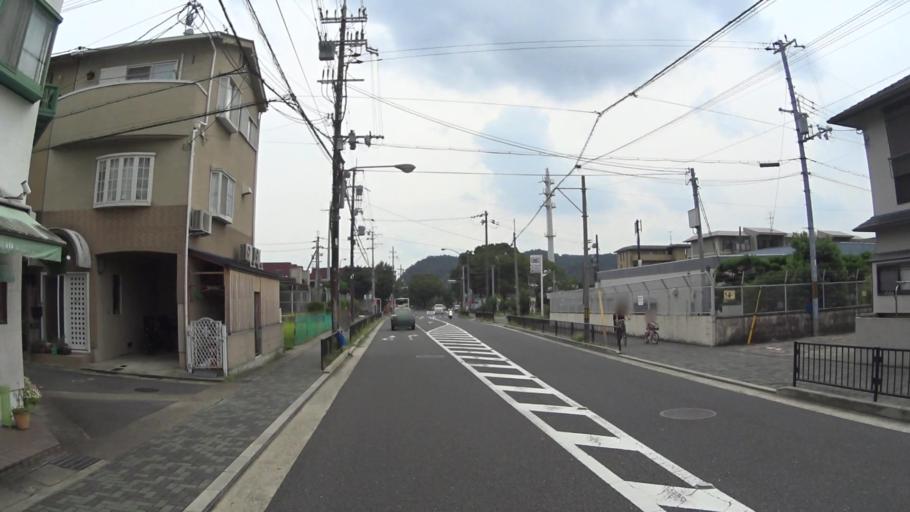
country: JP
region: Kyoto
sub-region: Kyoto-shi
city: Kamigyo-ku
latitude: 35.0650
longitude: 135.7926
